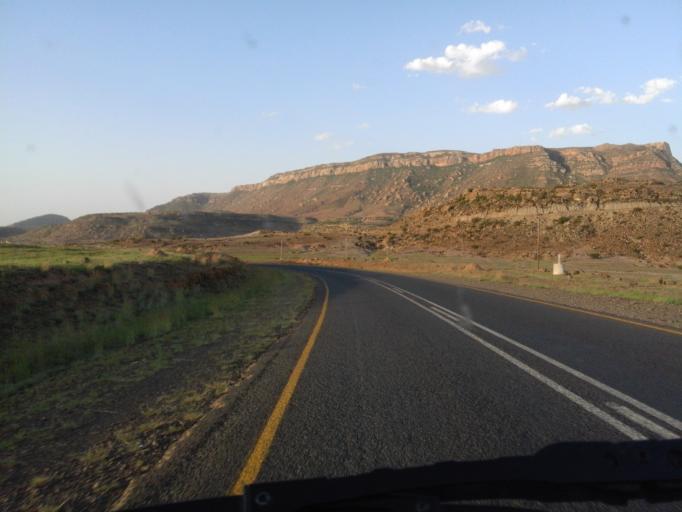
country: LS
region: Mafeteng
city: Mafeteng
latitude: -29.8953
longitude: 27.2557
